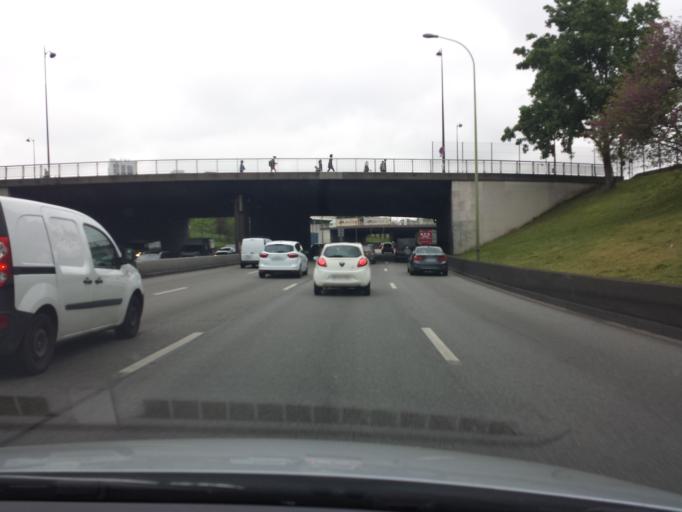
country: FR
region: Ile-de-France
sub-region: Departement de Seine-Saint-Denis
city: Bagnolet
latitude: 48.8530
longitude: 2.4146
